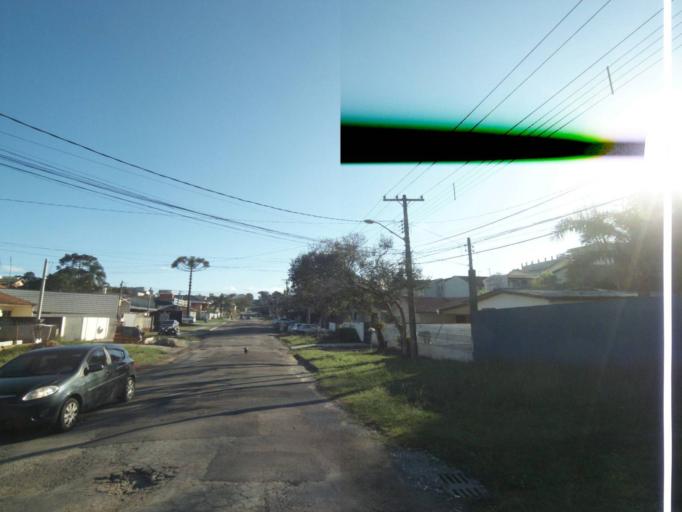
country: BR
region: Parana
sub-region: Curitiba
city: Curitiba
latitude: -25.3848
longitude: -49.2512
